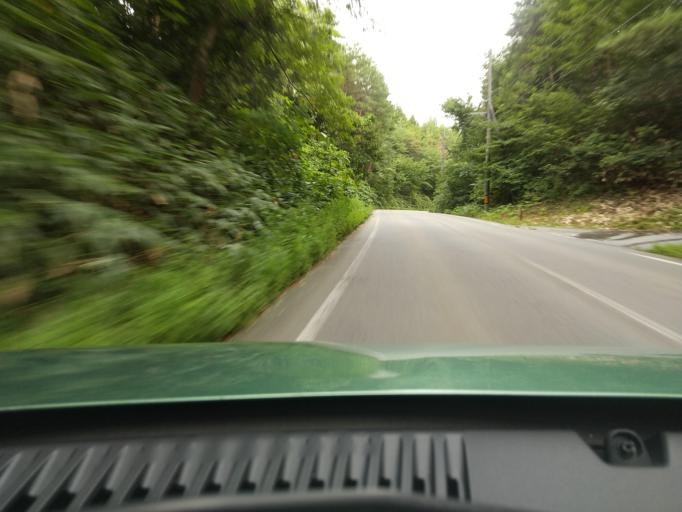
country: JP
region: Akita
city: Akita
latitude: 39.7736
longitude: 140.1337
